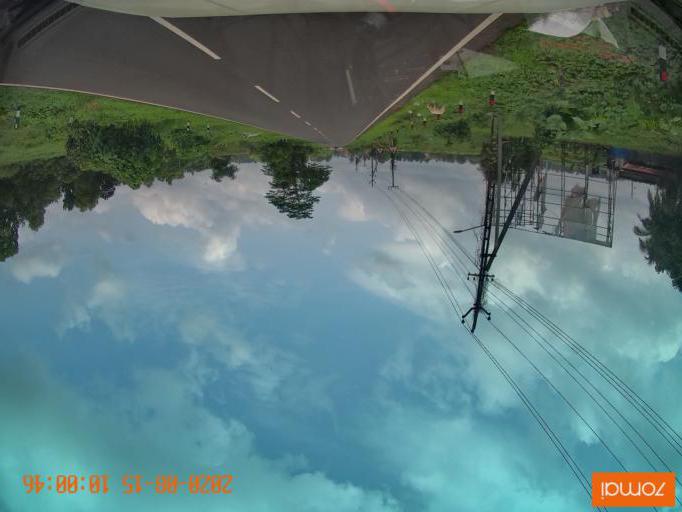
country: IN
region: Kerala
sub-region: Kottayam
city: Changanacheri
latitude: 9.4343
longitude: 76.5481
